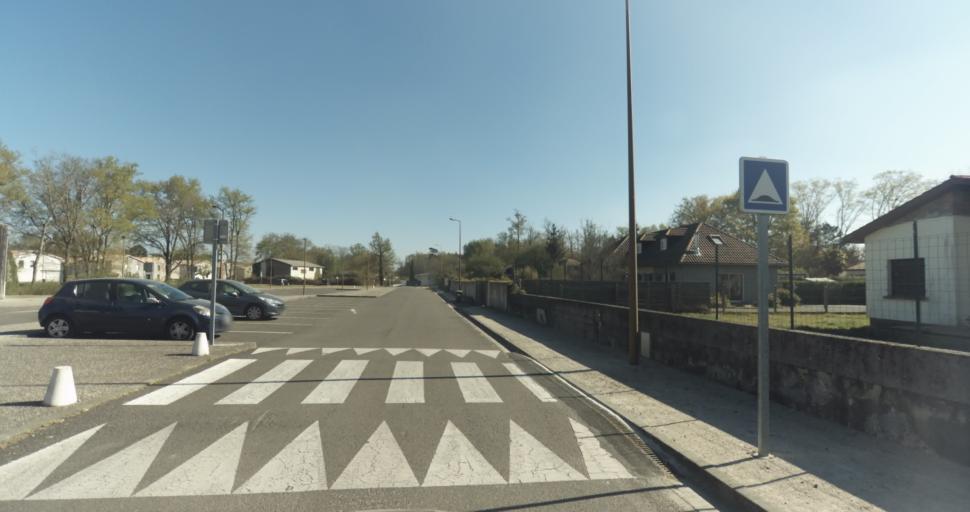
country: FR
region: Aquitaine
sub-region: Departement de la Gironde
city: Martignas-sur-Jalle
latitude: 44.7974
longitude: -0.8370
